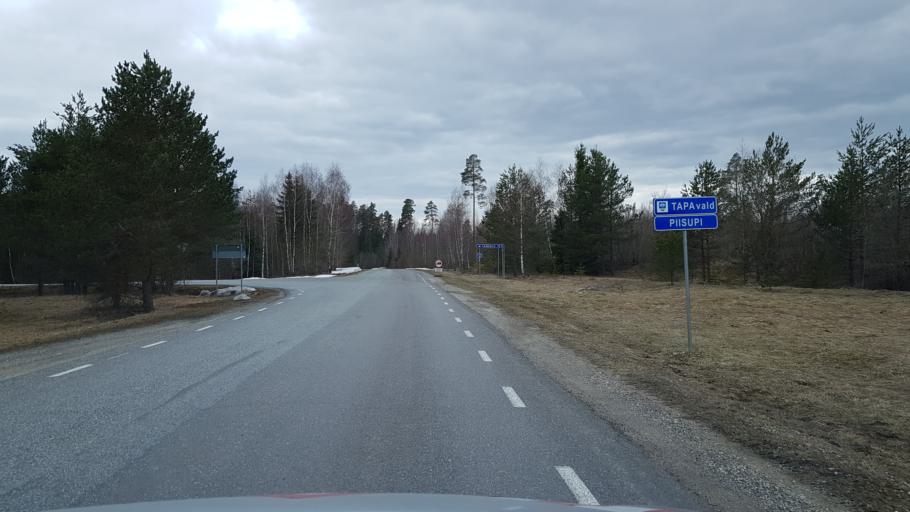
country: EE
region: Laeaene-Virumaa
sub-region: Kadrina vald
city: Kadrina
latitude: 59.2403
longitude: 26.1779
